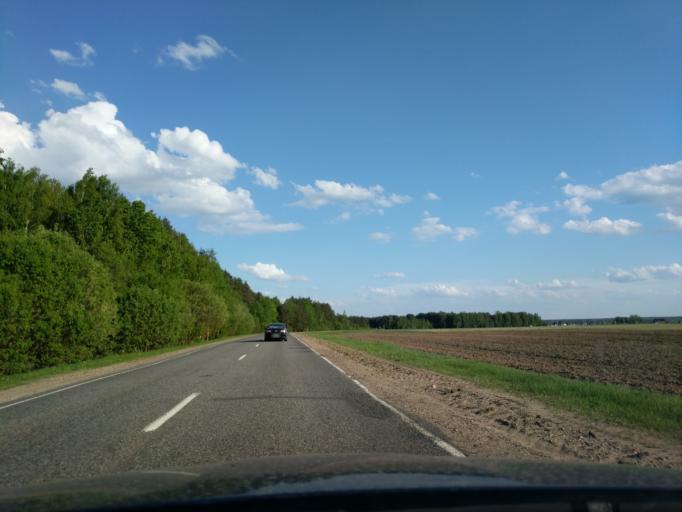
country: BY
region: Minsk
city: Il'ya
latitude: 54.5201
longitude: 27.2225
